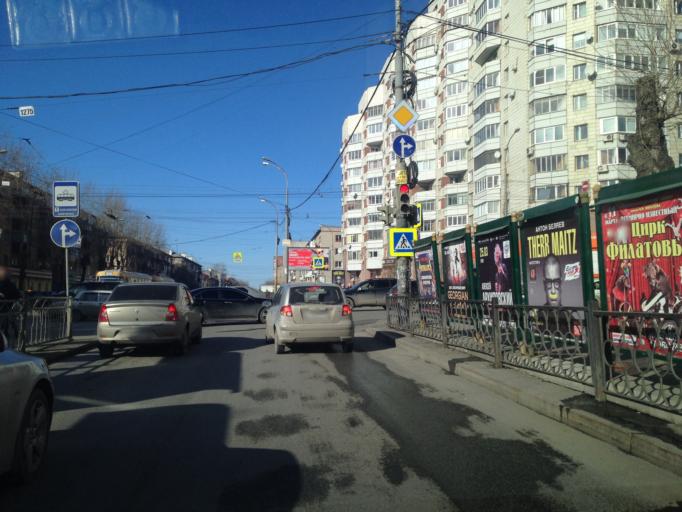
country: RU
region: Sverdlovsk
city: Yekaterinburg
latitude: 56.8485
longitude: 60.6174
